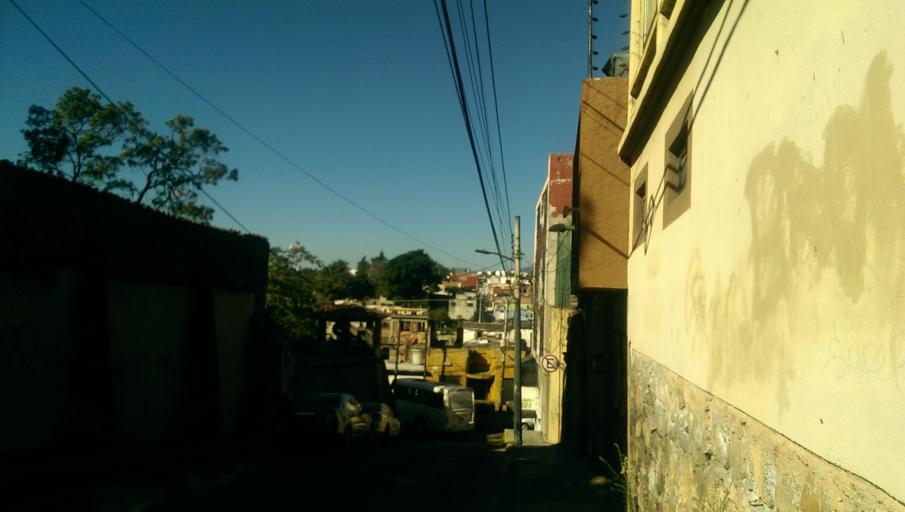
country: MX
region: Morelos
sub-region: Cuernavaca
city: Cuernavaca
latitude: 18.9230
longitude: -99.2391
